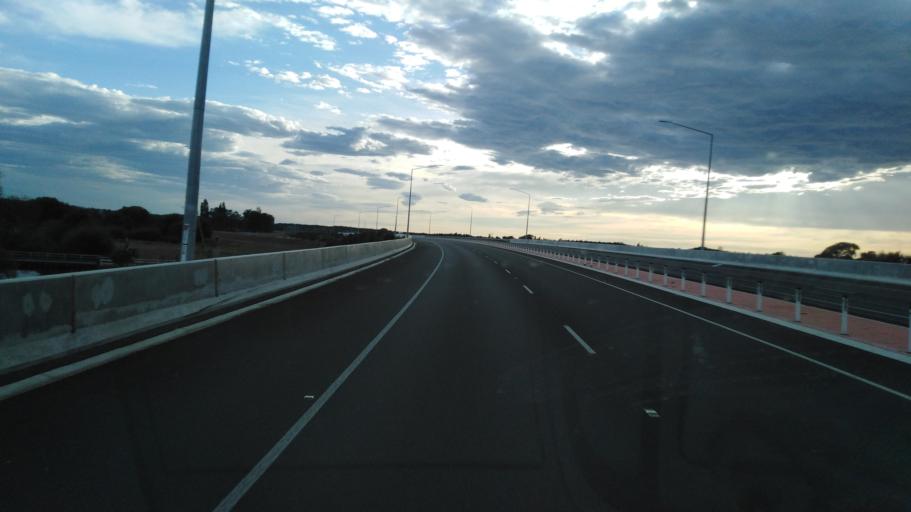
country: NZ
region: Canterbury
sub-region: Waimakariri District
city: Kaiapoi
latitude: -43.4364
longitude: 172.6340
